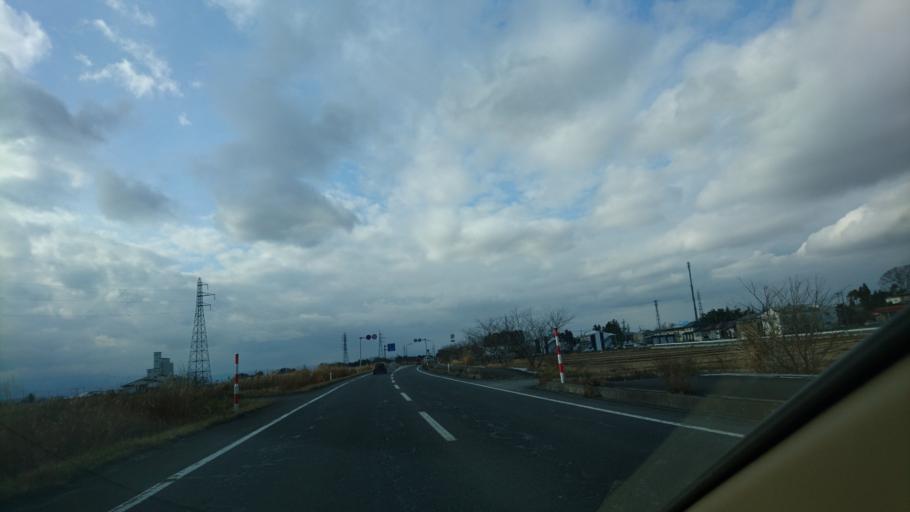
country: JP
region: Miyagi
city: Kogota
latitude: 38.5526
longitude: 141.0520
